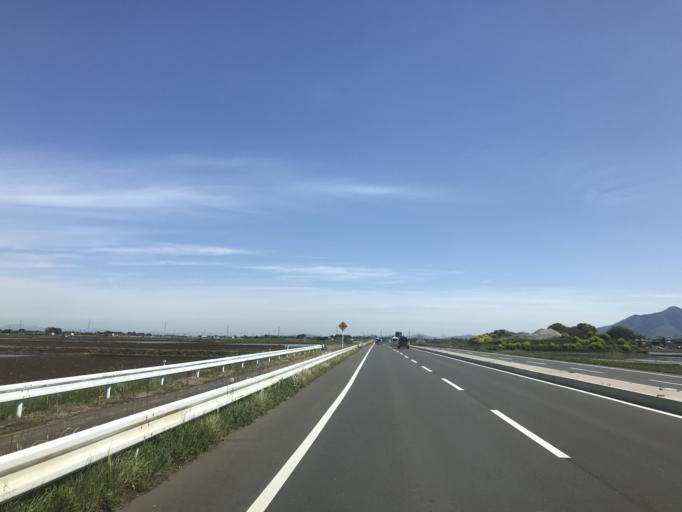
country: JP
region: Ibaraki
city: Ishige
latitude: 36.1418
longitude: 139.9881
